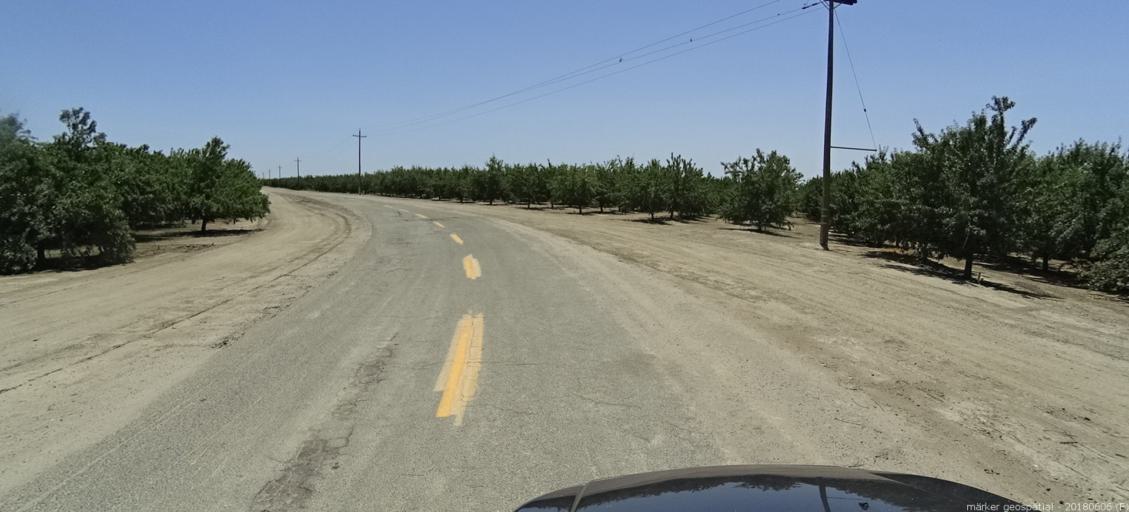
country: US
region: California
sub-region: Fresno County
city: Mendota
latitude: 36.8035
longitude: -120.3401
